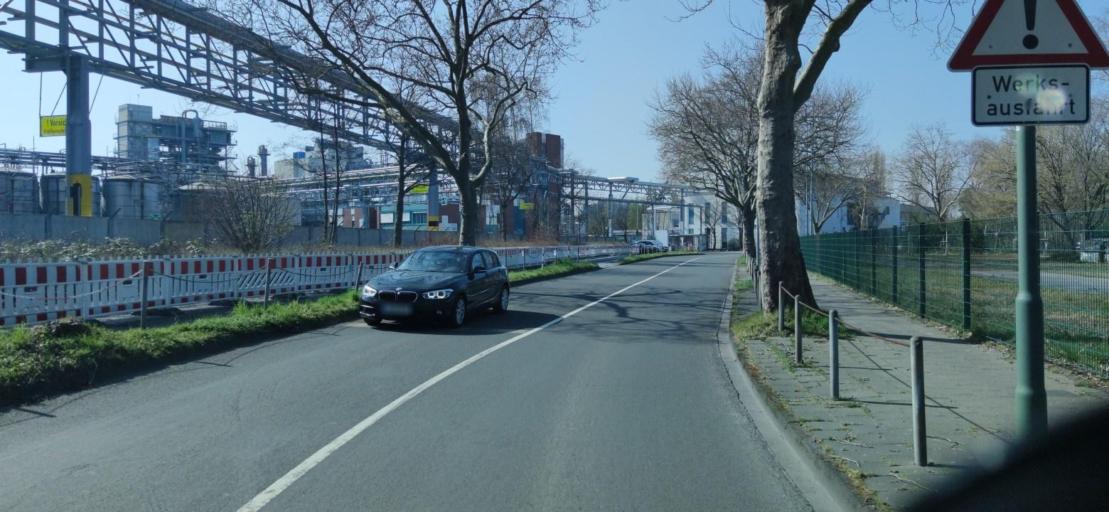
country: DE
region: North Rhine-Westphalia
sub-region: Regierungsbezirk Dusseldorf
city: Dusseldorf
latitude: 51.1826
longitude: 6.8387
